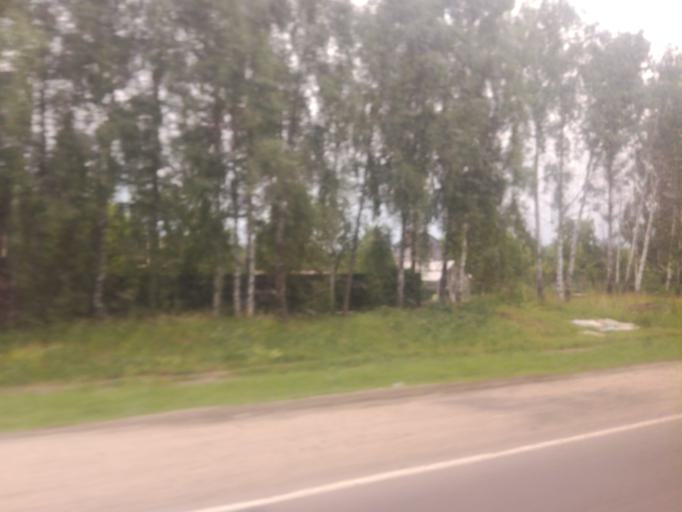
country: RU
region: Kursk
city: Kursk
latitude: 51.7539
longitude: 36.1060
